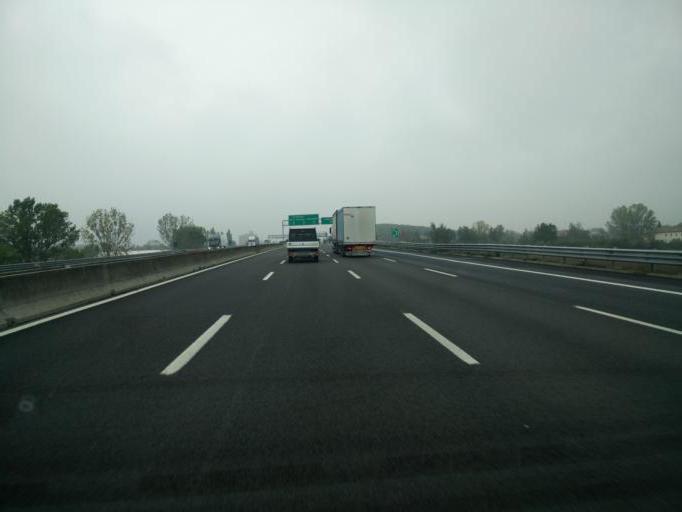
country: IT
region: Emilia-Romagna
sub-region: Provincia di Modena
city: Baggiovara
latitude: 44.6423
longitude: 10.8702
